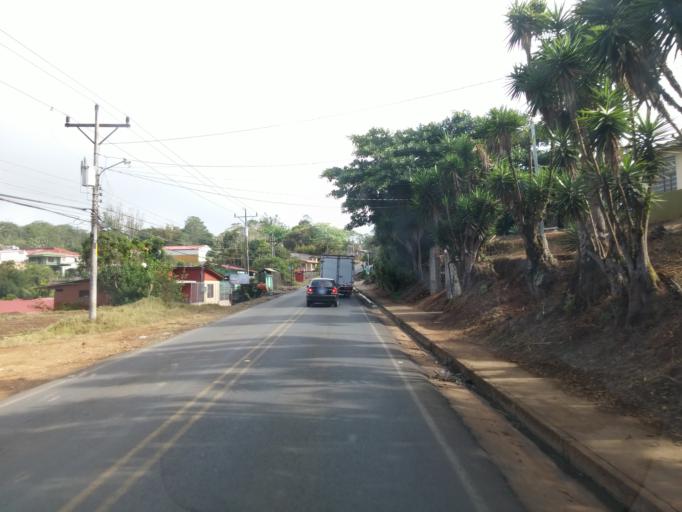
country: CR
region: Alajuela
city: San Ramon
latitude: 10.1105
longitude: -84.4690
